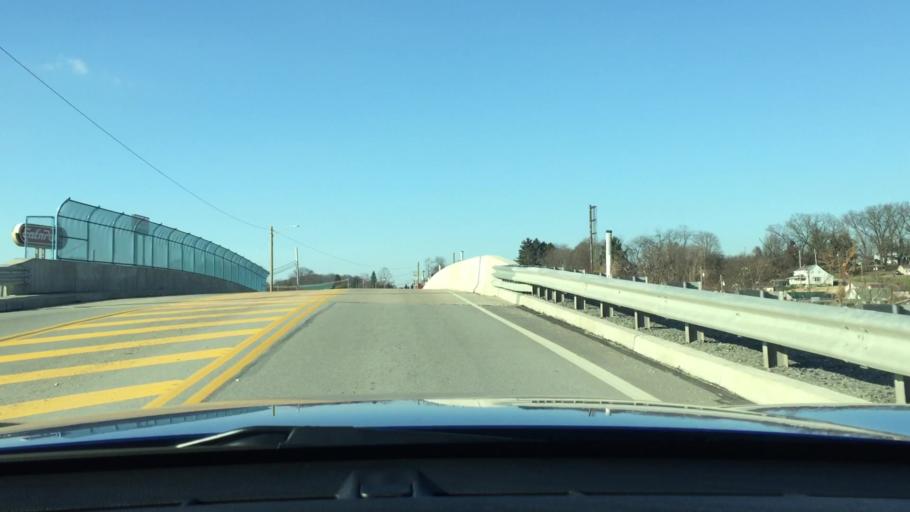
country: US
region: Pennsylvania
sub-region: Westmoreland County
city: New Stanton
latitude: 40.2173
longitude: -79.6082
